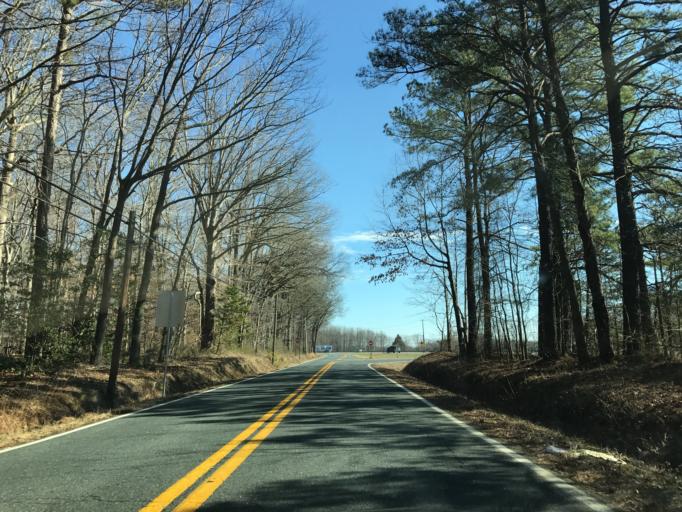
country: US
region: Maryland
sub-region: Queen Anne's County
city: Grasonville
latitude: 38.9810
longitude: -76.1409
